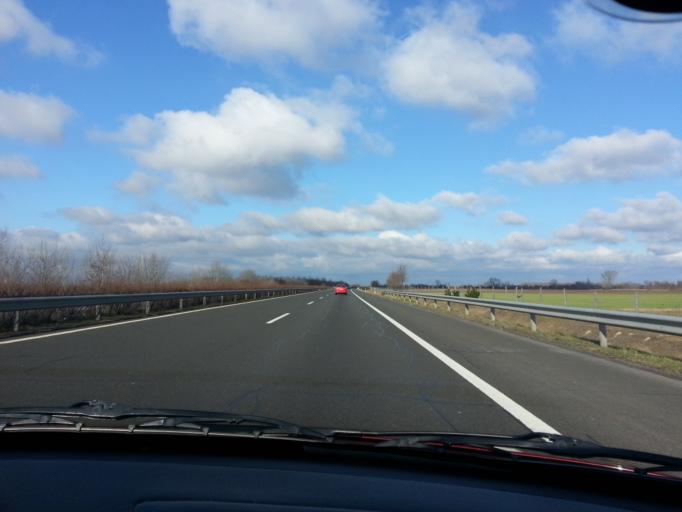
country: HU
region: Csongrad
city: Balastya
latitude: 46.4188
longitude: 19.9570
